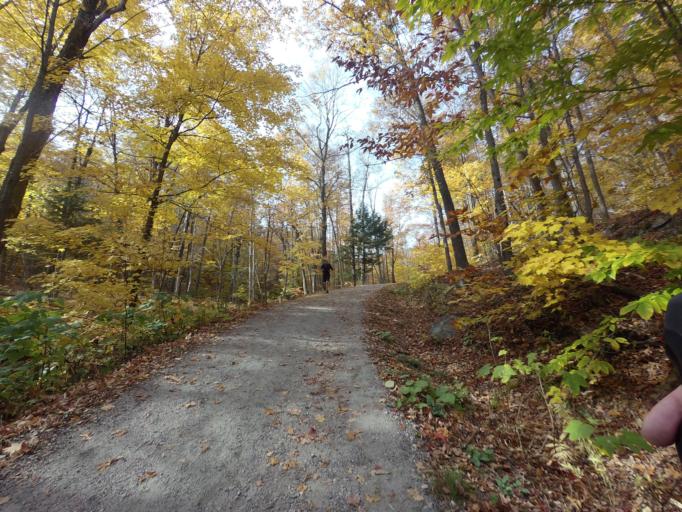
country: CA
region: Quebec
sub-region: Outaouais
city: Gatineau
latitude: 45.4989
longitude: -75.8360
